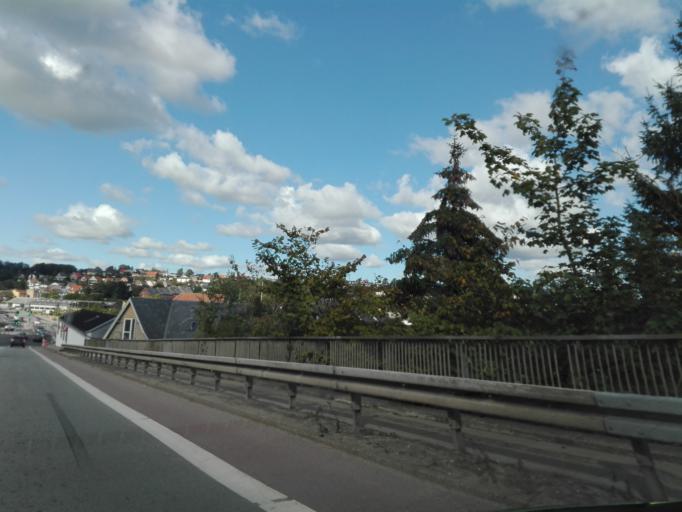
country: DK
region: North Denmark
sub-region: Mariagerfjord Kommune
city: Hobro
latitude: 56.6372
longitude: 9.7993
